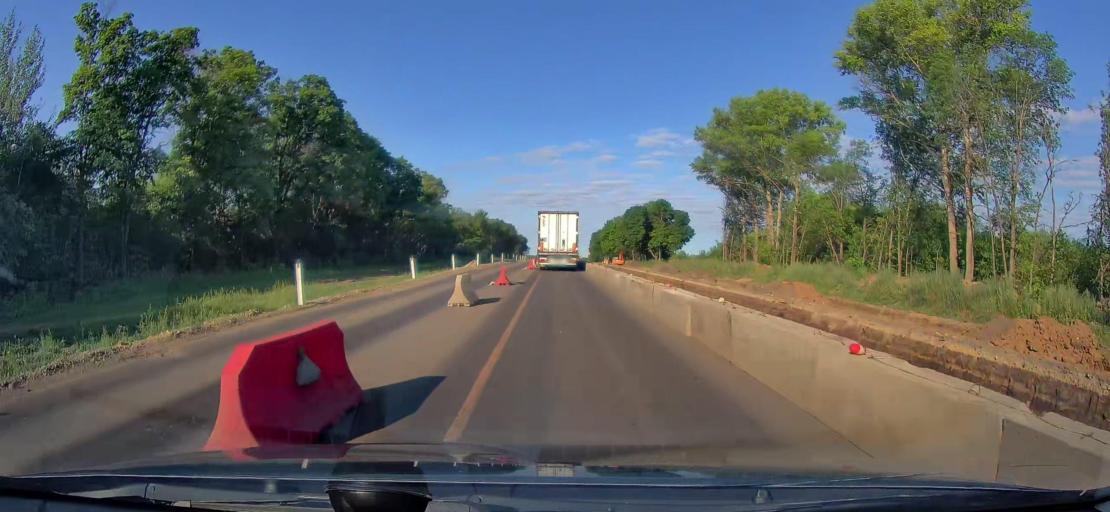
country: RU
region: Tula
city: Bol'shoye Skuratovo
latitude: 53.4468
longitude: 36.8442
